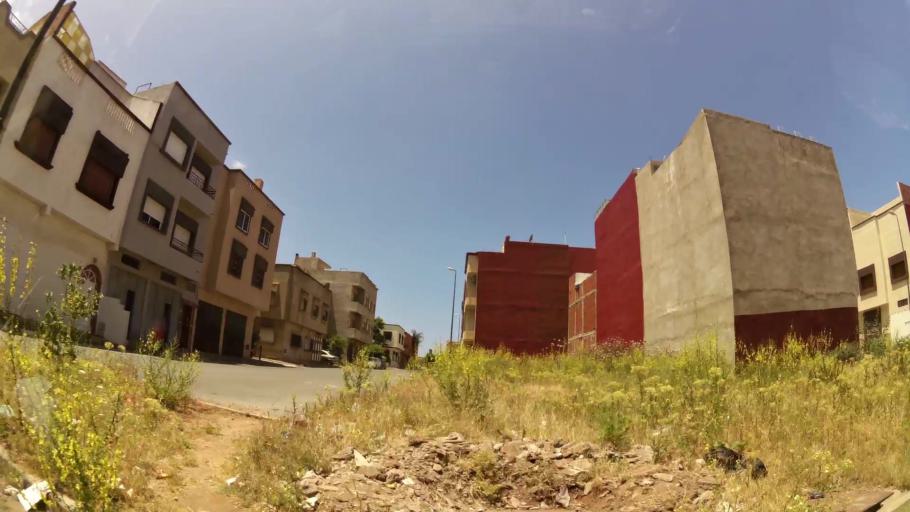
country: MA
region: Gharb-Chrarda-Beni Hssen
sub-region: Kenitra Province
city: Kenitra
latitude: 34.2703
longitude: -6.6178
